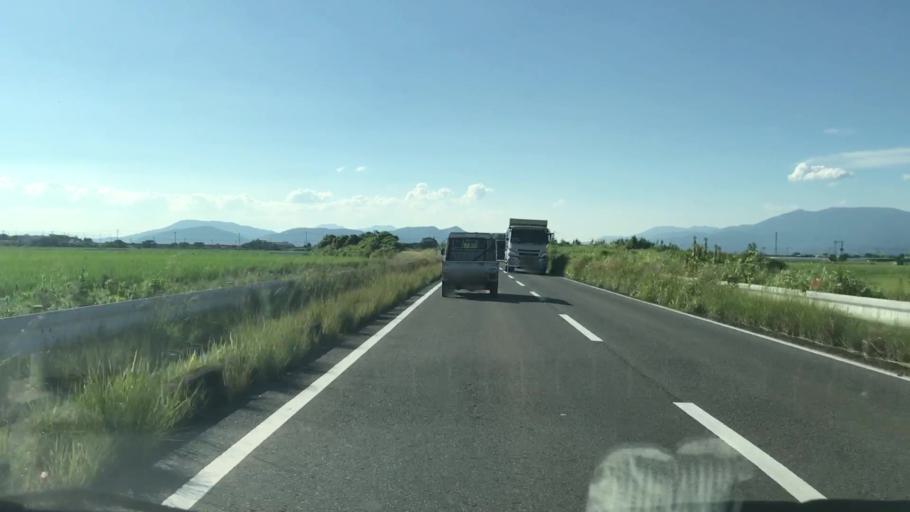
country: JP
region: Saga Prefecture
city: Saga-shi
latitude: 33.2078
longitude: 130.2676
